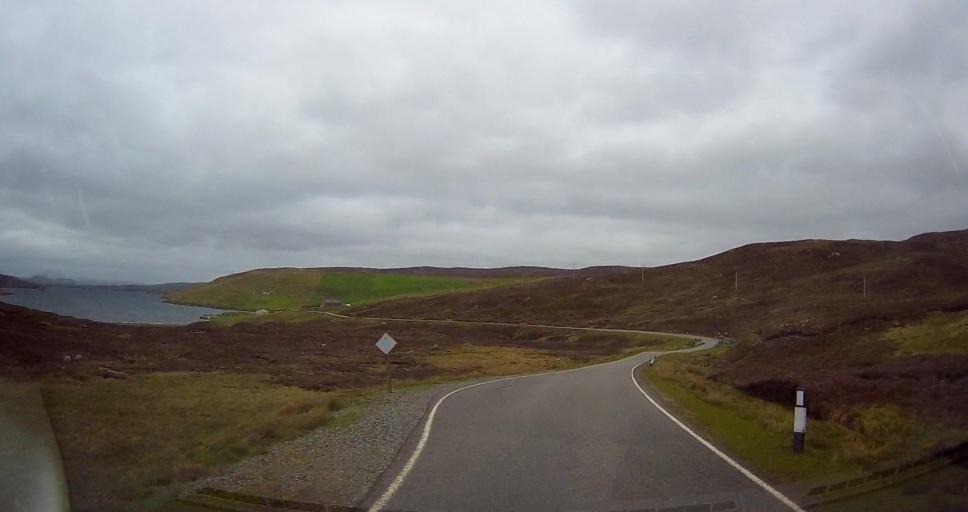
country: GB
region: Scotland
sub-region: Shetland Islands
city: Lerwick
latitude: 60.3291
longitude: -1.3375
